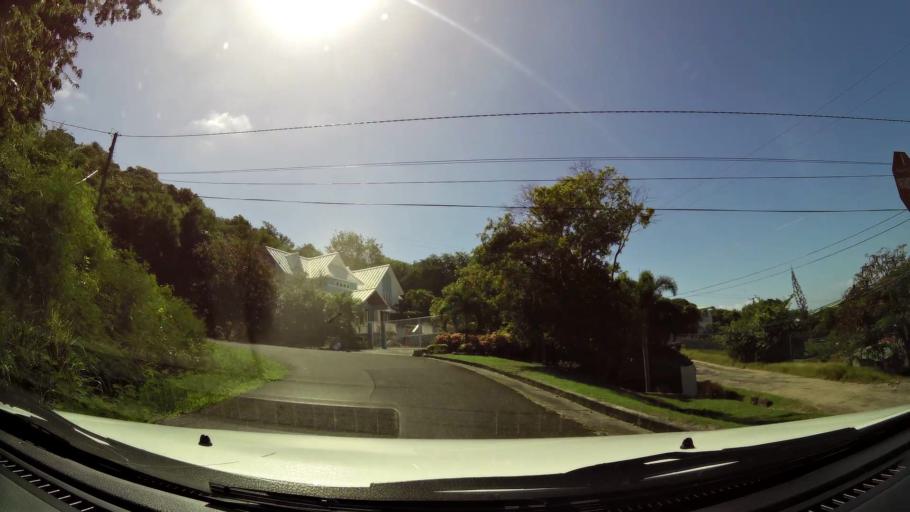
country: LC
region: Vieux-Fort
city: Vieux Fort
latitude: 13.7186
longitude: -60.9498
